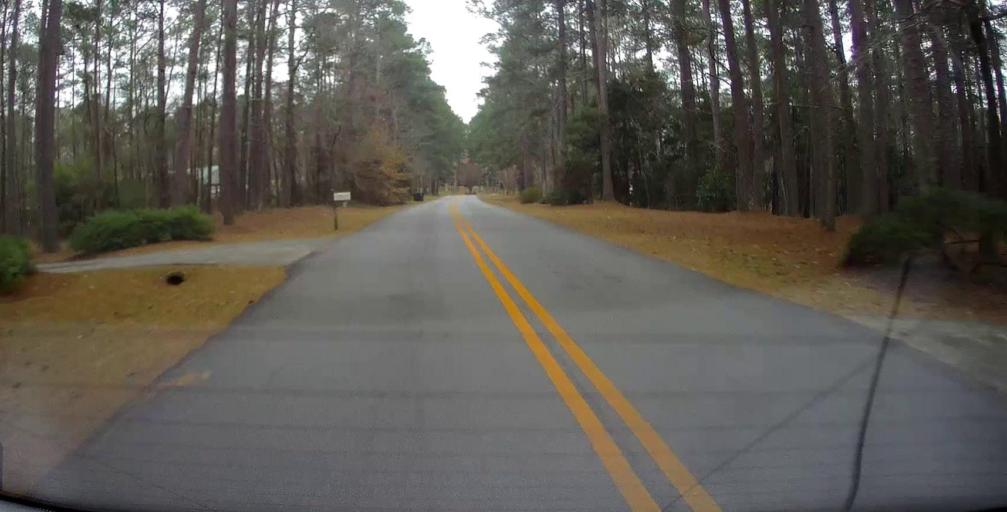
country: US
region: Georgia
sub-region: Bibb County
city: West Point
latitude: 32.9096
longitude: -83.7510
